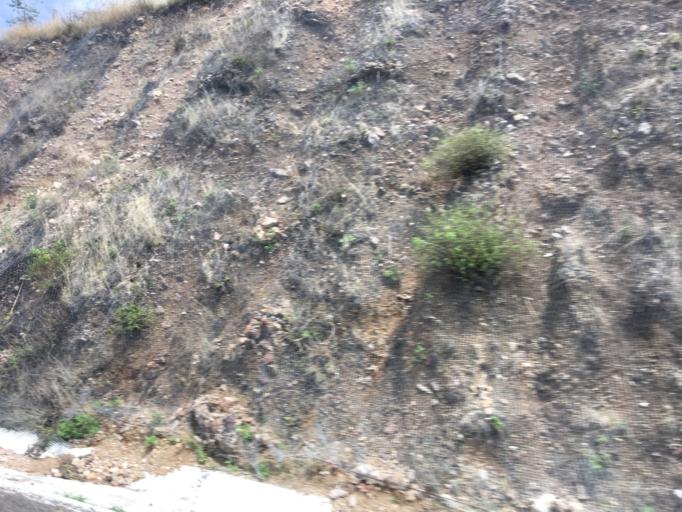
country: MX
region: Guanajuato
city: Santa Teresa
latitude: 20.9683
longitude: -101.3221
